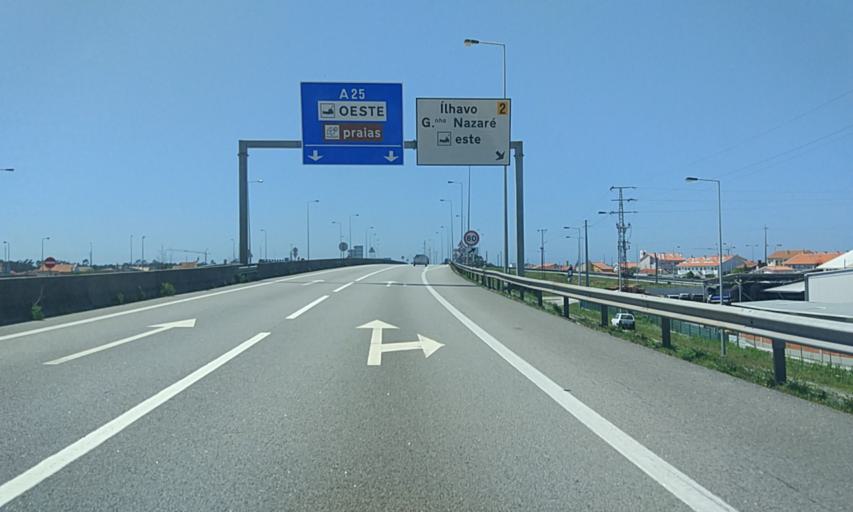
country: PT
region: Aveiro
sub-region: Ilhavo
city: Gafanha da Nazare
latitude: 40.6319
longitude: -8.6872
